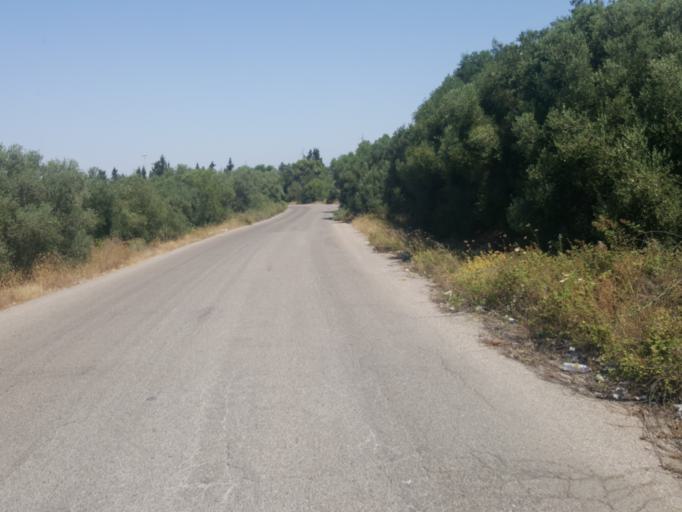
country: IT
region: Apulia
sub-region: Provincia di Taranto
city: Statte
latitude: 40.5050
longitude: 17.1943
